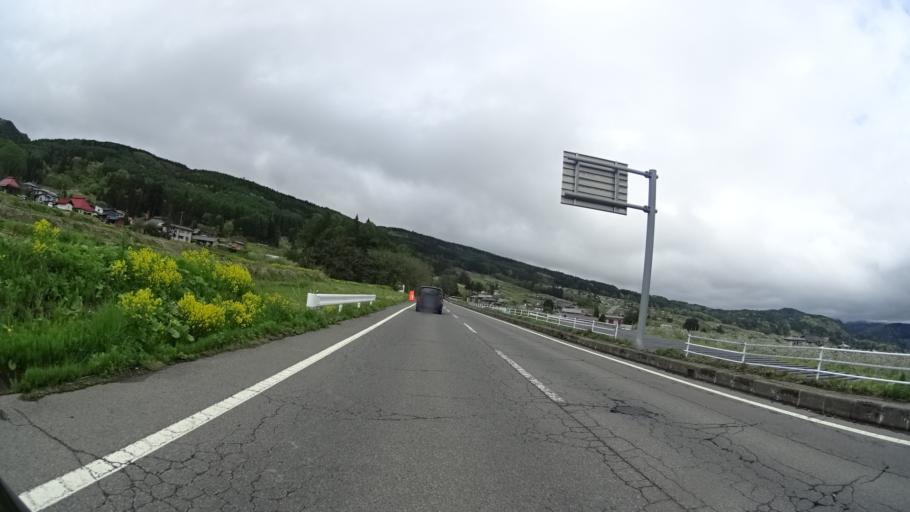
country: JP
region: Nagano
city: Nagano-shi
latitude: 36.7335
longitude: 138.2076
